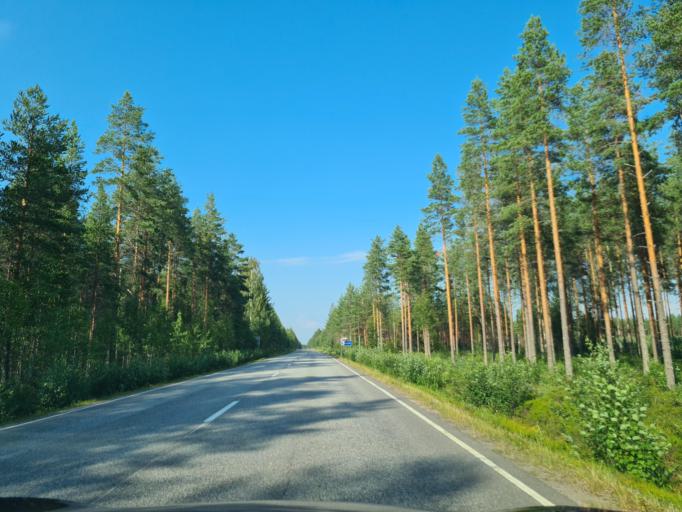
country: FI
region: Satakunta
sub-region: Pohjois-Satakunta
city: Karvia
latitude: 62.3002
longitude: 22.6331
